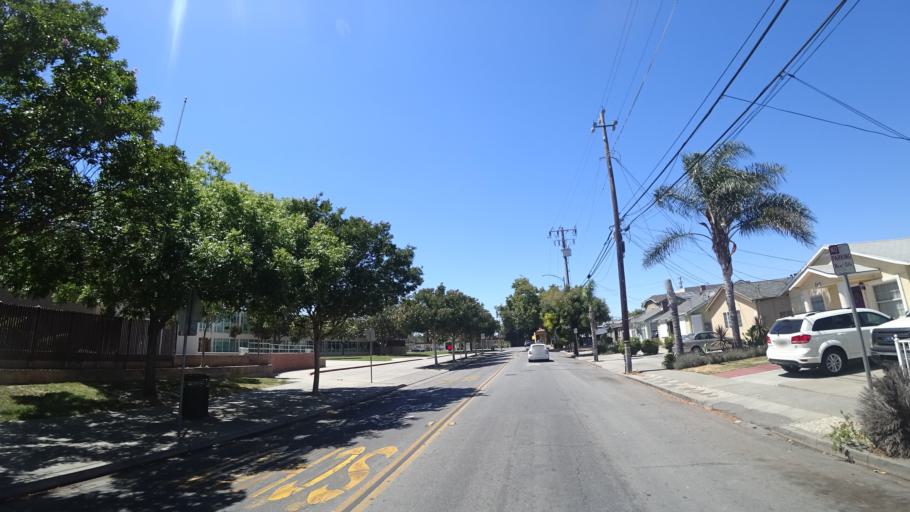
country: US
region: California
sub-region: Santa Clara County
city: San Jose
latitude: 37.3500
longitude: -121.8706
